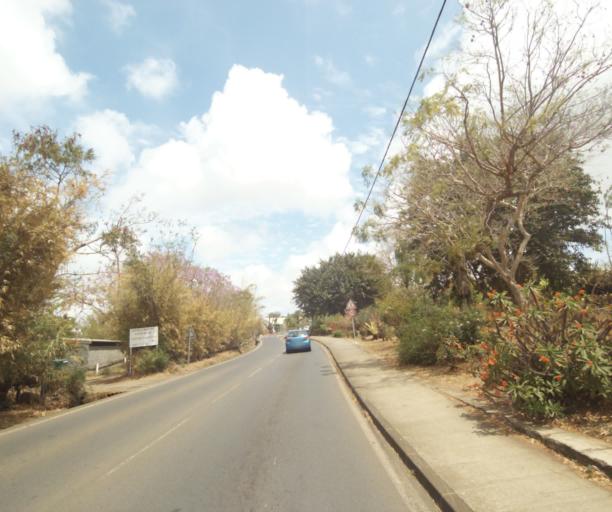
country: RE
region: Reunion
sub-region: Reunion
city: Saint-Paul
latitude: -21.0448
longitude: 55.2682
